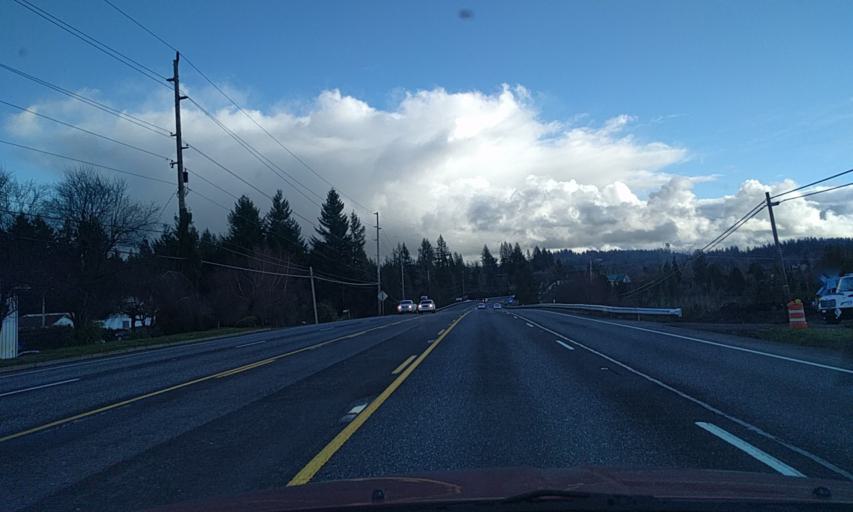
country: US
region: Oregon
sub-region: Clackamas County
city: Sandy
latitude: 45.3828
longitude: -122.2303
